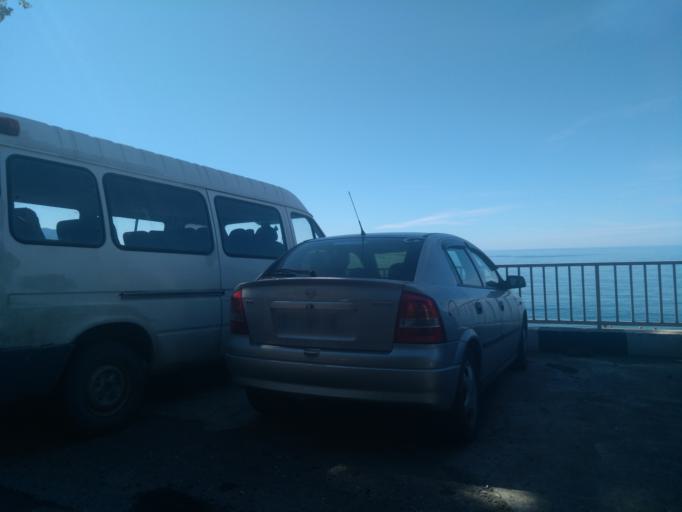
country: TR
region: Artvin
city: Kemalpasa
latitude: 41.5251
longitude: 41.5490
